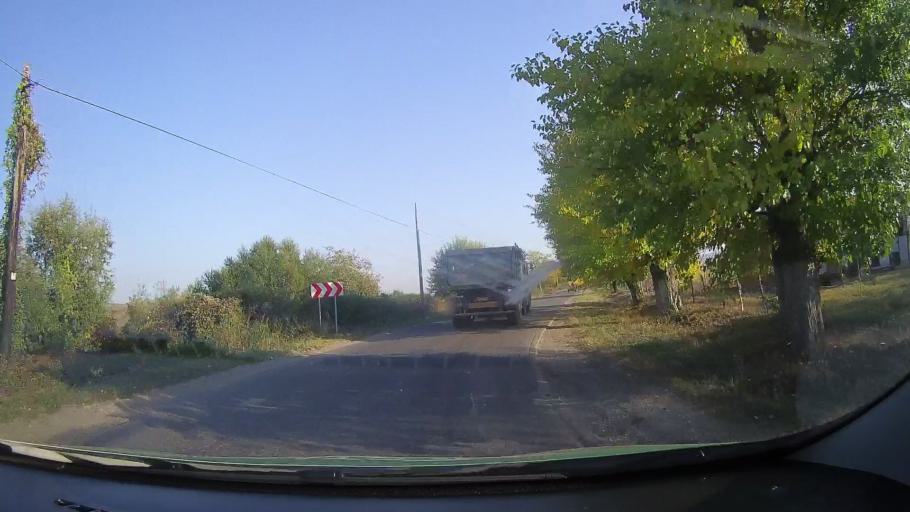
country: RO
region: Arad
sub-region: Comuna Pancota
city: Pancota
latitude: 46.3163
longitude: 21.7000
